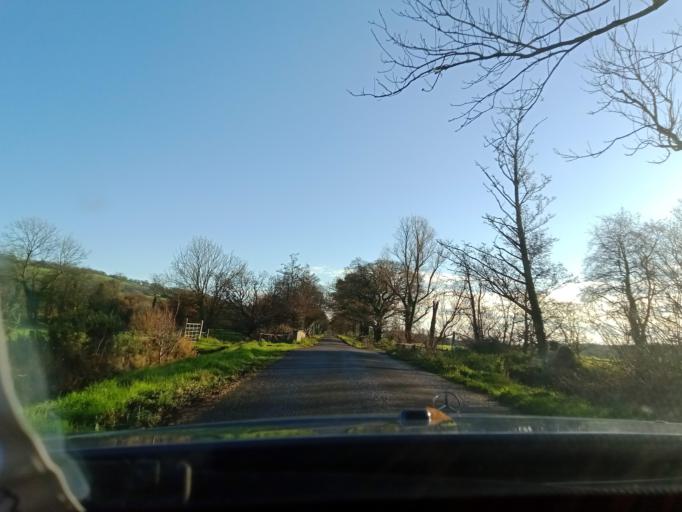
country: IE
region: Leinster
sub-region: Kilkenny
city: Piltown
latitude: 52.3522
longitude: -7.2894
